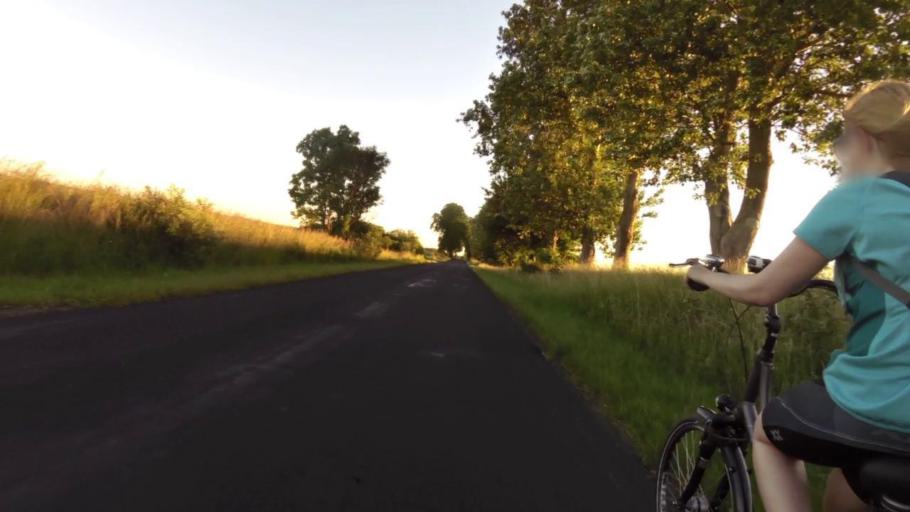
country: PL
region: West Pomeranian Voivodeship
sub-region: Powiat bialogardzki
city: Bialogard
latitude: 54.0279
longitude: 16.0286
